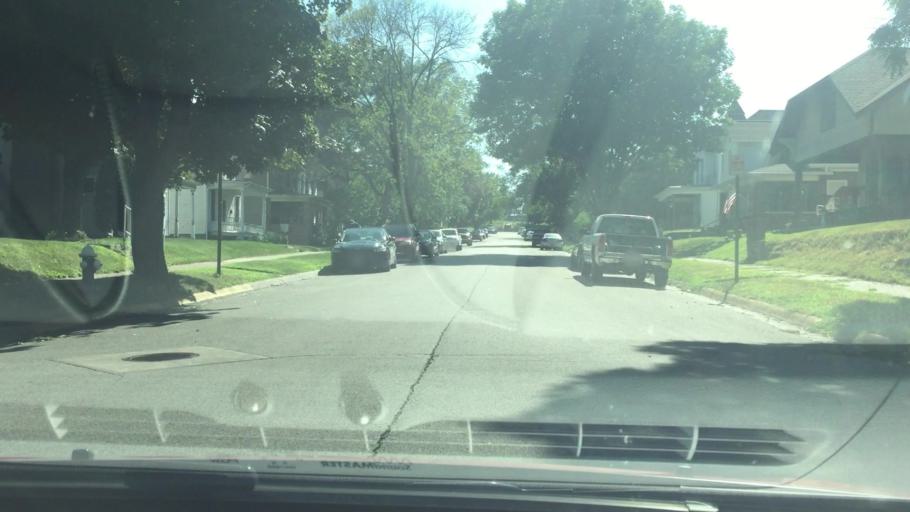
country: US
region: Iowa
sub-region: Muscatine County
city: Muscatine
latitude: 41.4211
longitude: -91.0505
